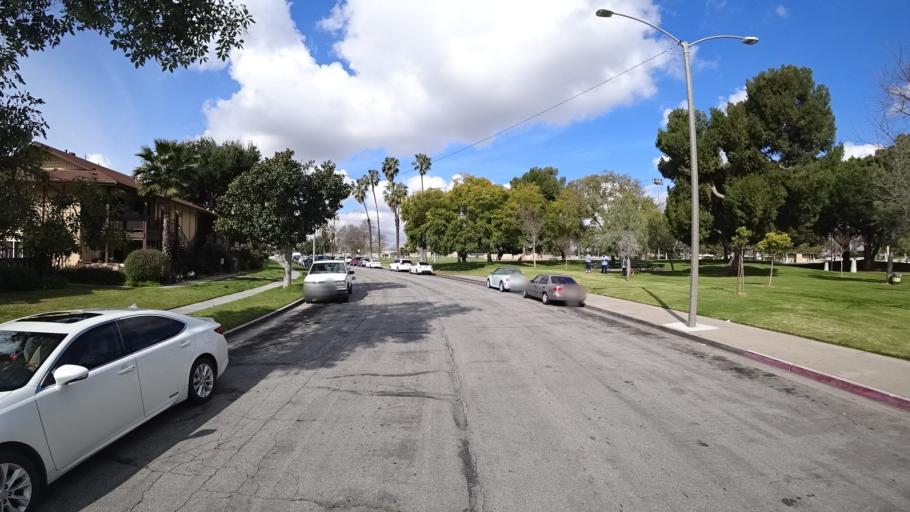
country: US
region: California
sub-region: Orange County
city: Buena Park
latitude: 33.8419
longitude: -117.9636
